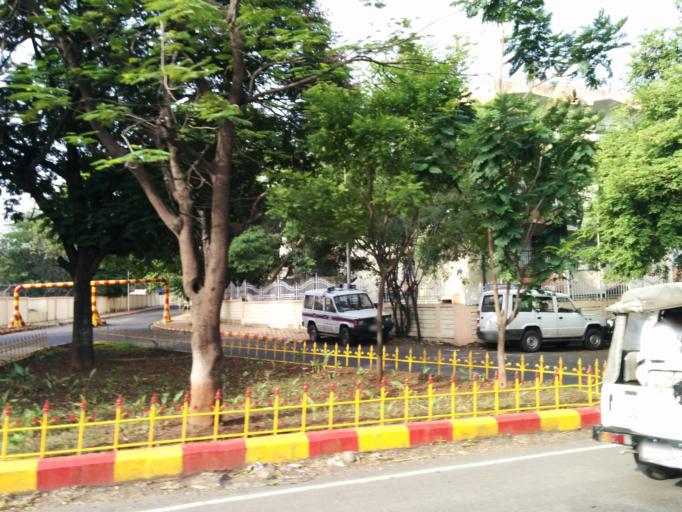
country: IN
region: Maharashtra
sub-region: Pune Division
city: Pune
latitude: 18.5064
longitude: 73.8898
